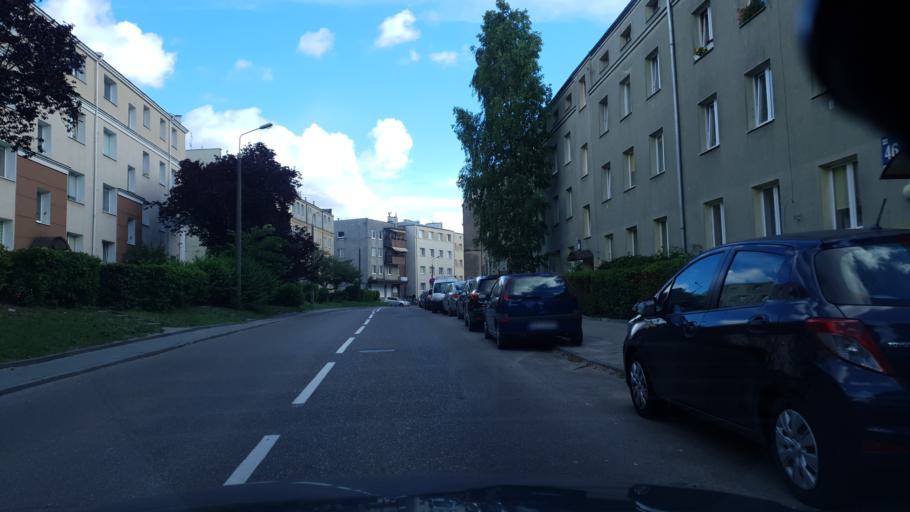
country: PL
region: Pomeranian Voivodeship
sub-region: Gdynia
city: Gdynia
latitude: 54.5048
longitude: 18.5429
